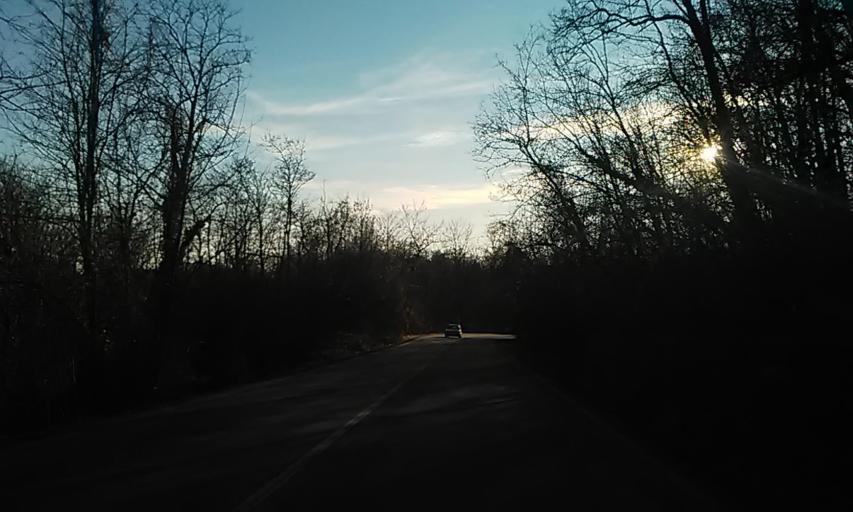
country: IT
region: Piedmont
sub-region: Provincia di Biella
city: Cossato
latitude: 45.5664
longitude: 8.2085
